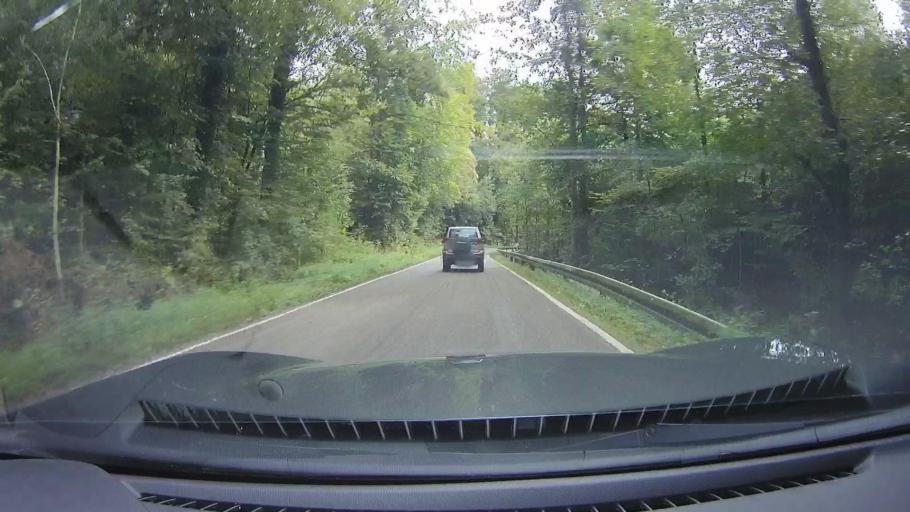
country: DE
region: Baden-Wuerttemberg
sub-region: Regierungsbezirk Stuttgart
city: Spiegelberg
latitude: 49.0481
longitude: 9.4177
